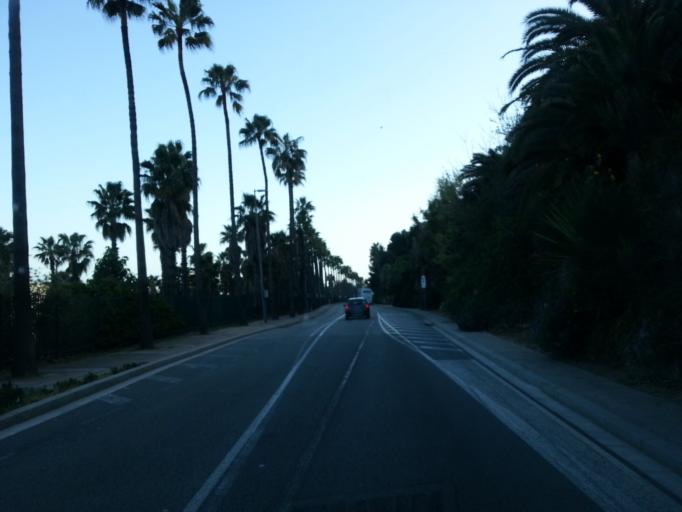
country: ES
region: Catalonia
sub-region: Provincia de Barcelona
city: Ciutat Vella
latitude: 41.3687
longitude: 2.1712
